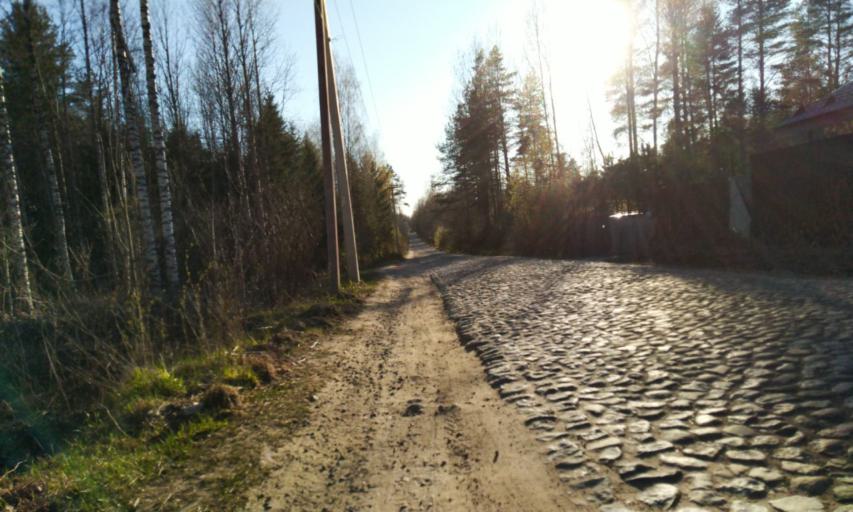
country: RU
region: Leningrad
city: Toksovo
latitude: 60.1398
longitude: 30.5612
